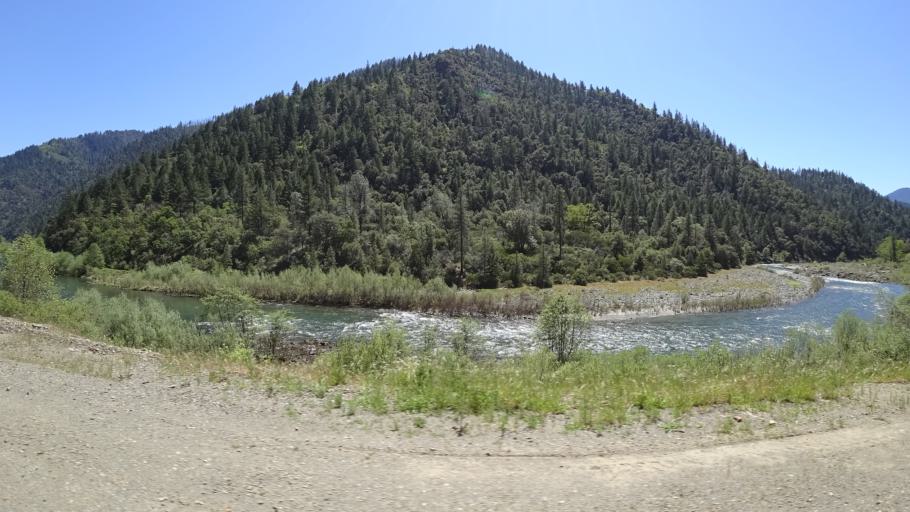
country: US
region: California
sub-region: Humboldt County
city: Willow Creek
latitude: 40.8008
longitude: -123.3909
